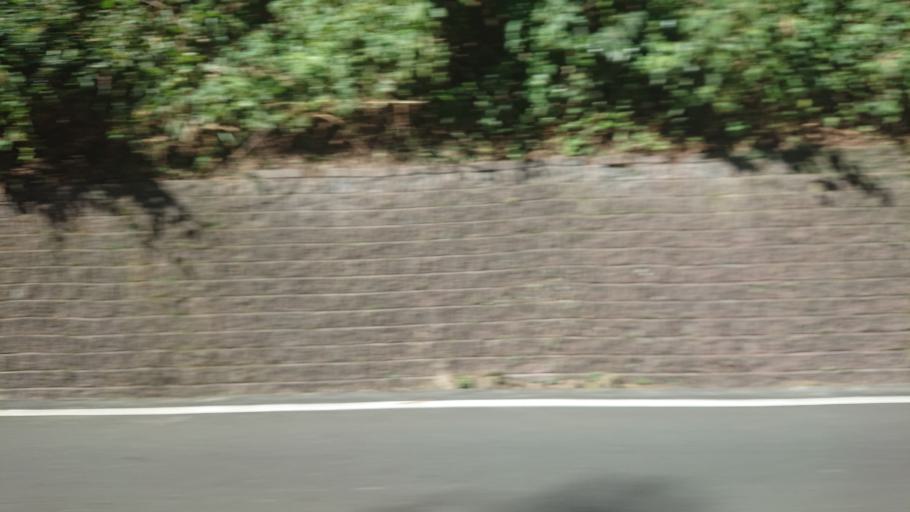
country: TW
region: Taiwan
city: Lugu
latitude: 23.4810
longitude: 120.7466
